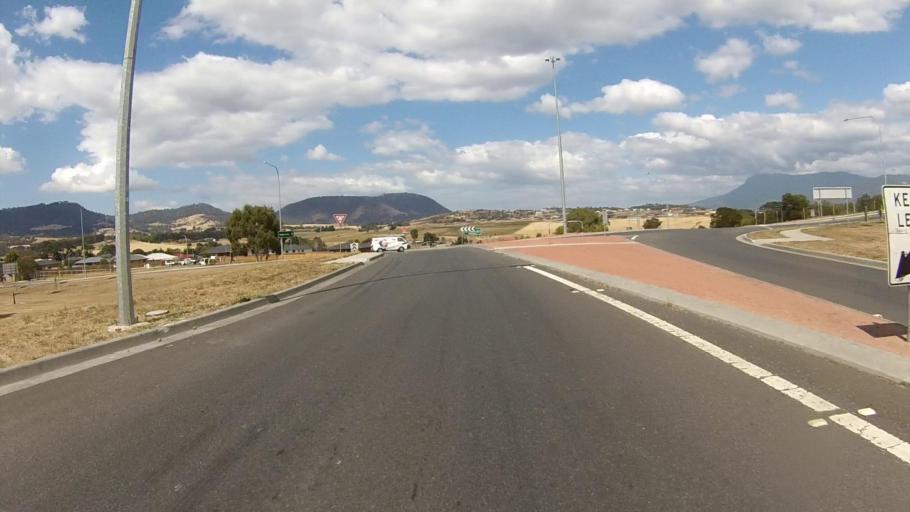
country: AU
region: Tasmania
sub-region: Glenorchy
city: Austins Ferry
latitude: -42.7505
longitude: 147.2723
